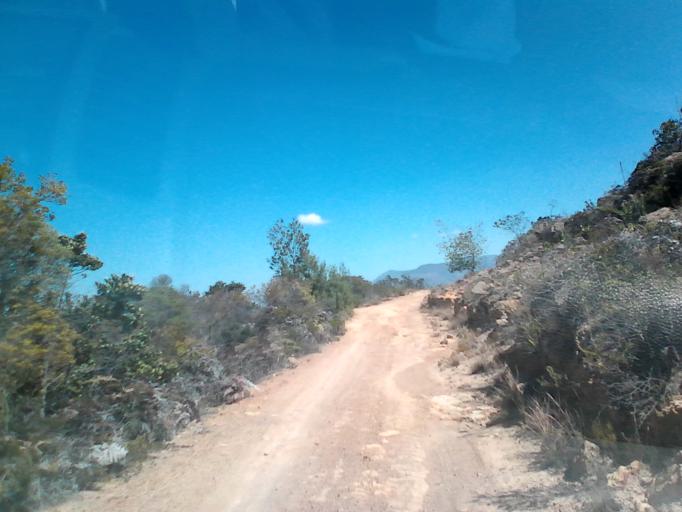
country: CO
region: Boyaca
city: Sachica
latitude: 5.5263
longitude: -73.5529
